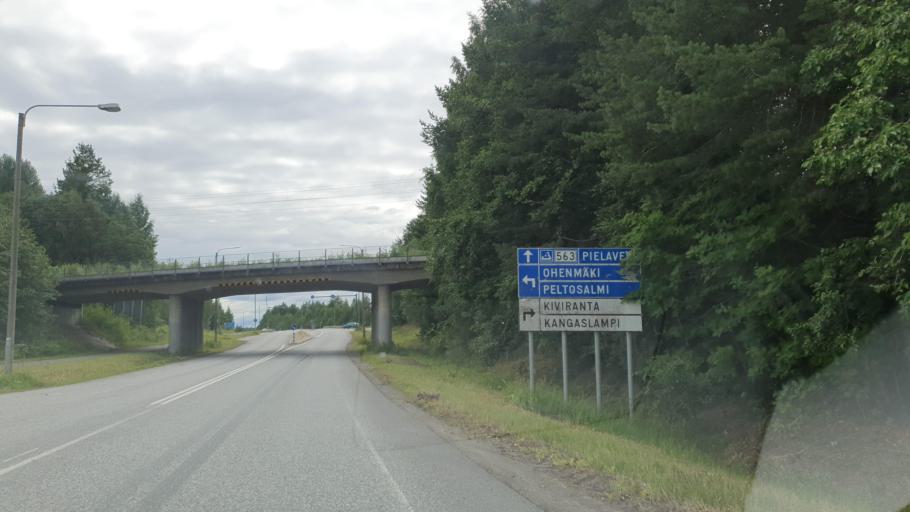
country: FI
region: Northern Savo
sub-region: Ylae-Savo
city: Iisalmi
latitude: 63.5236
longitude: 27.2453
